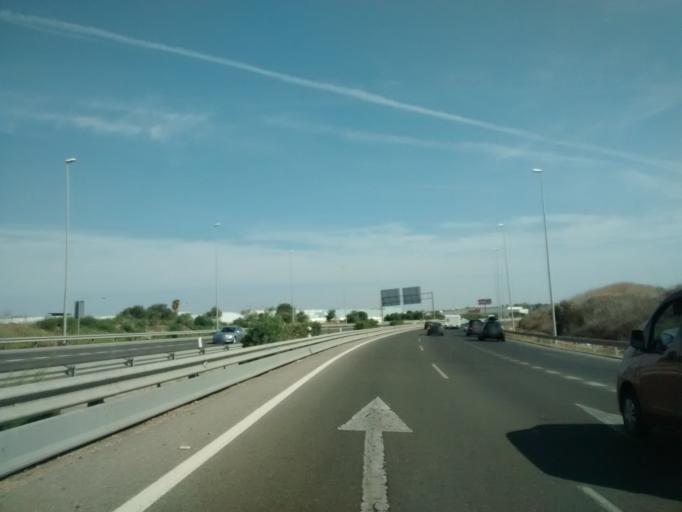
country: ES
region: Andalusia
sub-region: Provincia de Cadiz
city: Chiclana de la Frontera
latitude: 36.4015
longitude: -6.1262
